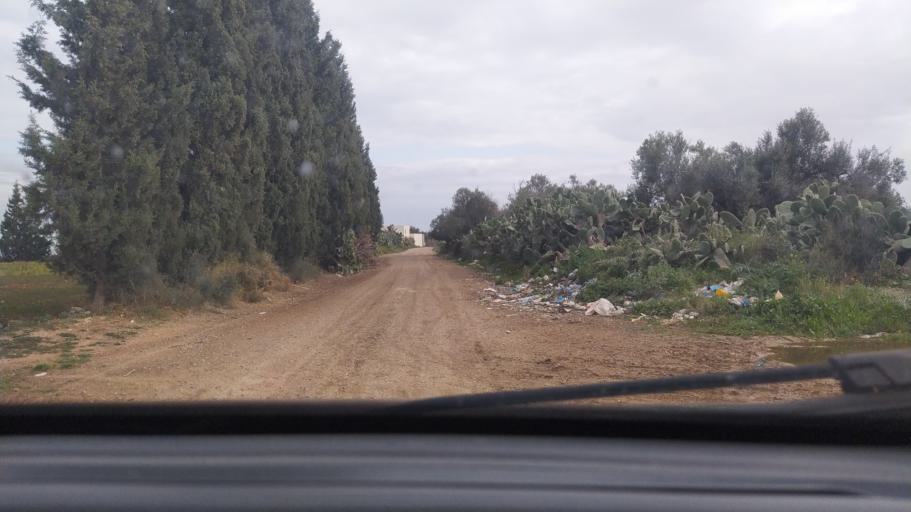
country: TN
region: Al Munastir
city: Sidi Bin Nur
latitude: 35.5163
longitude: 10.9299
